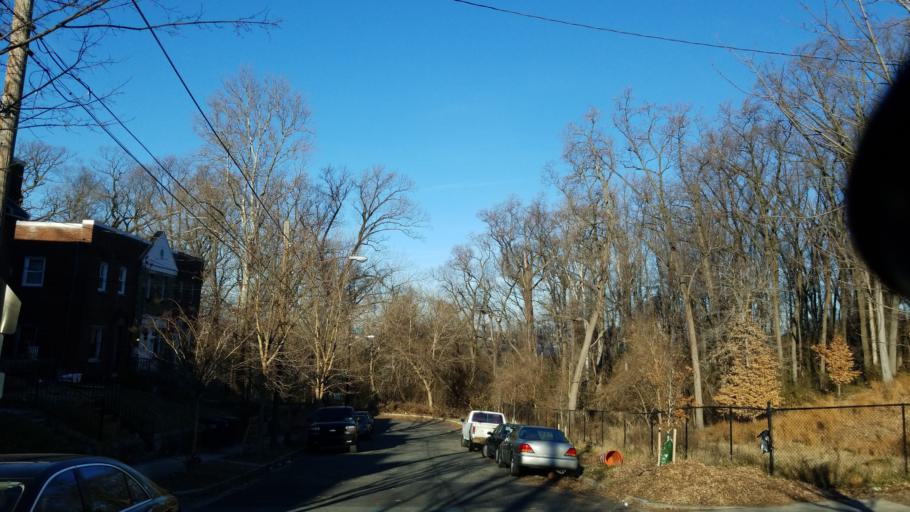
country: US
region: Maryland
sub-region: Prince George's County
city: Glassmanor
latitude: 38.8410
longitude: -77.0056
